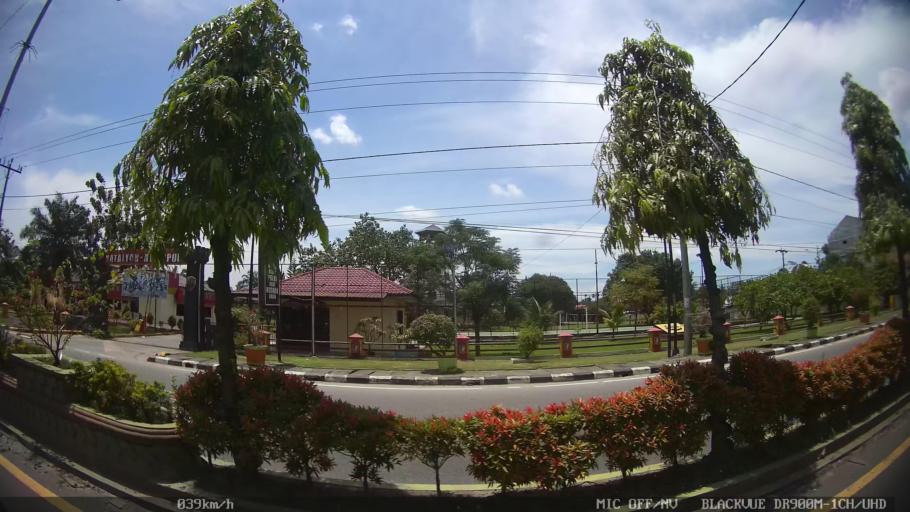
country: ID
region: North Sumatra
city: Binjai
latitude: 3.6086
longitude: 98.5046
